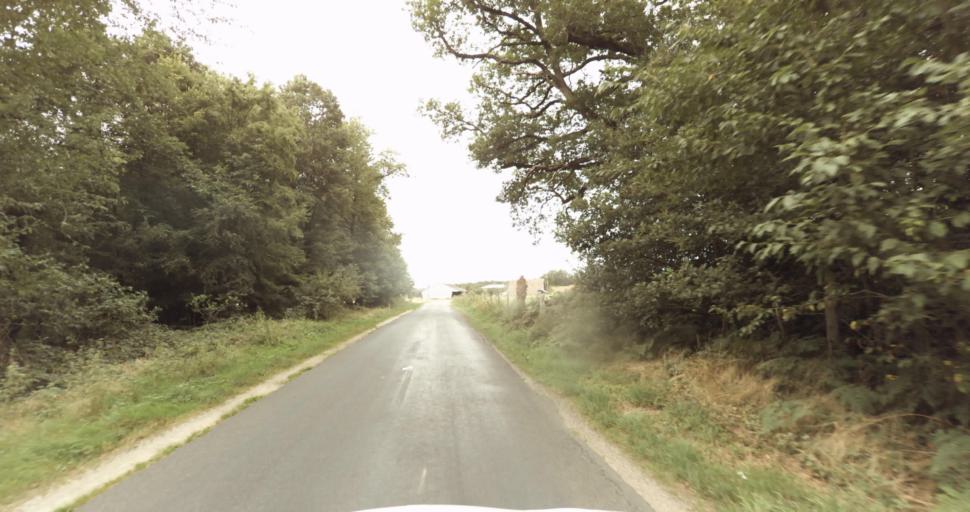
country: FR
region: Haute-Normandie
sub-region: Departement de l'Eure
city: Arnieres-sur-Iton
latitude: 48.9312
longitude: 1.1216
